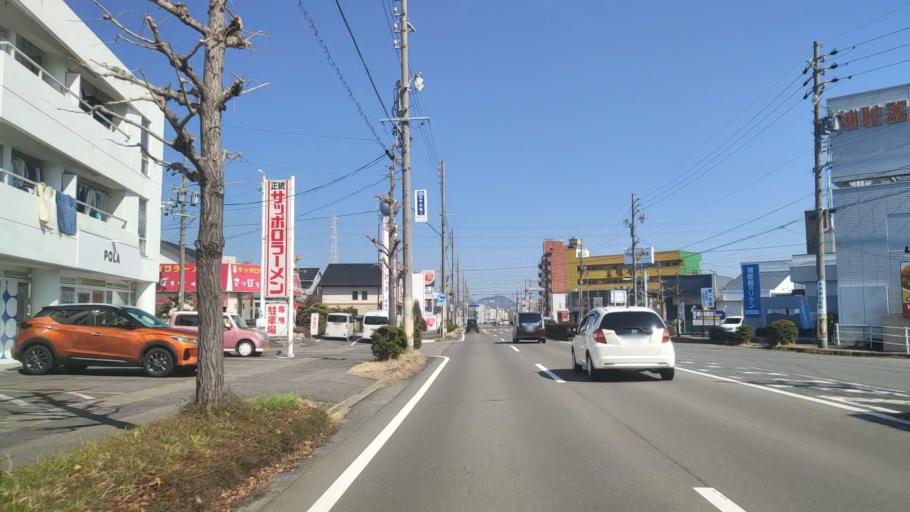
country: JP
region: Gifu
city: Gifu-shi
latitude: 35.3979
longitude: 136.7364
